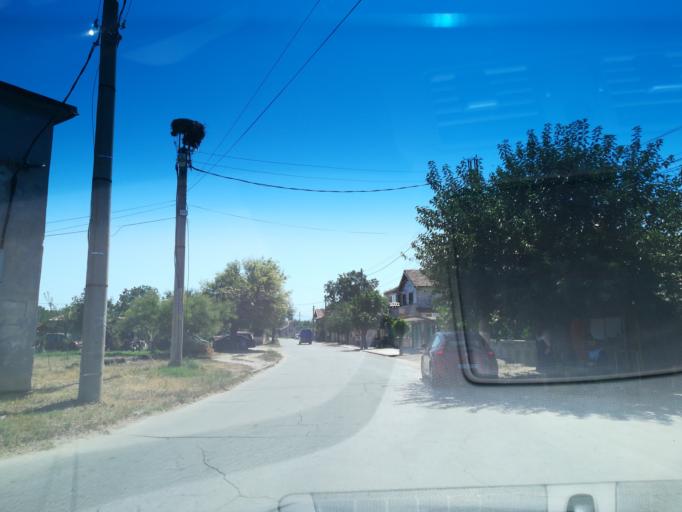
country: BG
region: Pazardzhik
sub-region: Obshtina Pazardzhik
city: Pazardzhik
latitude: 42.2796
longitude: 24.3949
